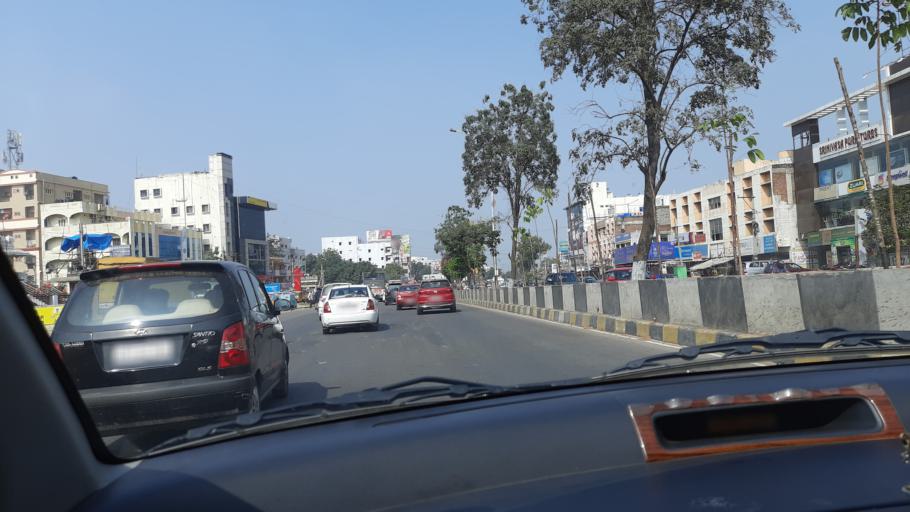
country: IN
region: Telangana
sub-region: Rangareddi
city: Lal Bahadur Nagar
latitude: 17.3634
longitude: 78.5572
